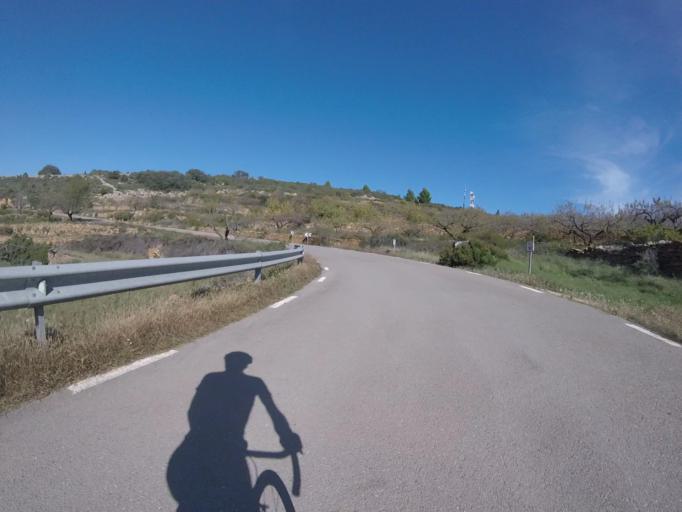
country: ES
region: Valencia
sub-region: Provincia de Castello
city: Sarratella
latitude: 40.2965
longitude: 0.0301
